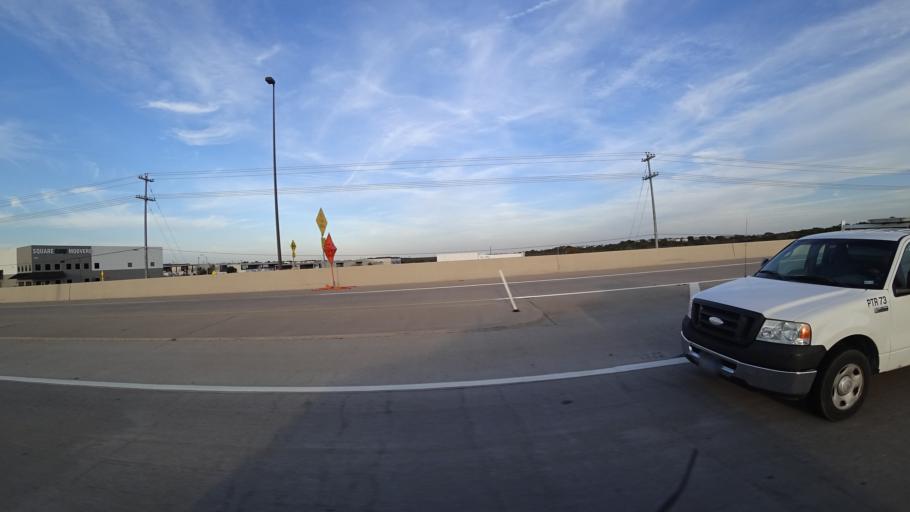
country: US
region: Texas
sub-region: Williamson County
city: Cedar Park
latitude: 30.4985
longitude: -97.8039
